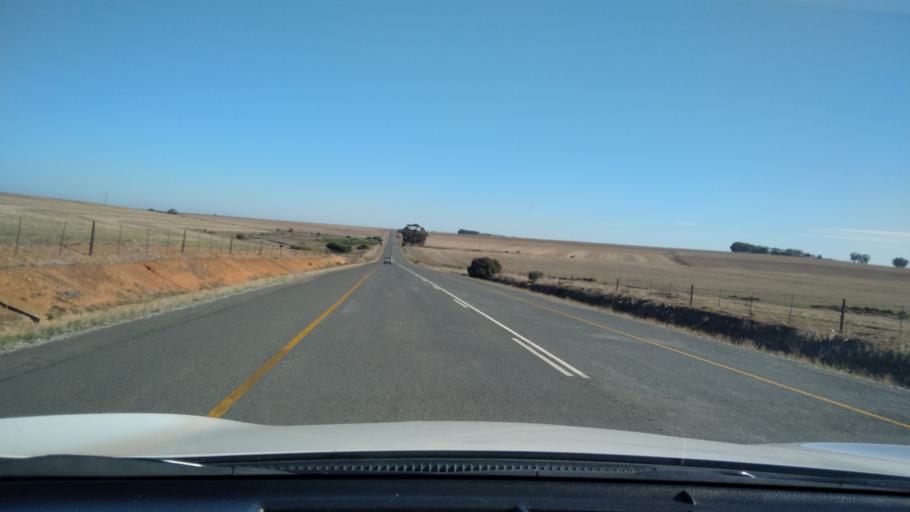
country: ZA
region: Western Cape
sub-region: West Coast District Municipality
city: Malmesbury
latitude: -33.3507
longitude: 18.6415
